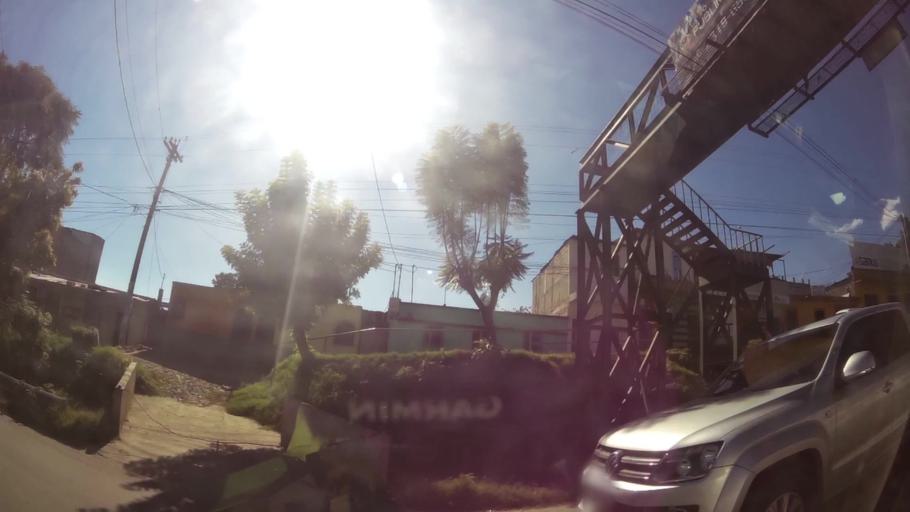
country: GT
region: Guatemala
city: Villa Nueva
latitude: 14.5474
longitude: -90.6190
